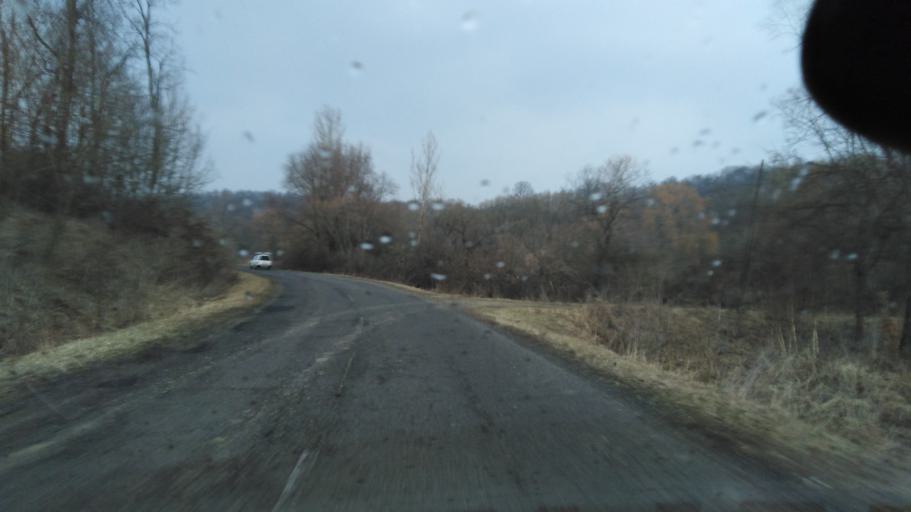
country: HU
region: Nograd
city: Salgotarjan
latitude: 48.0460
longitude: 19.7531
